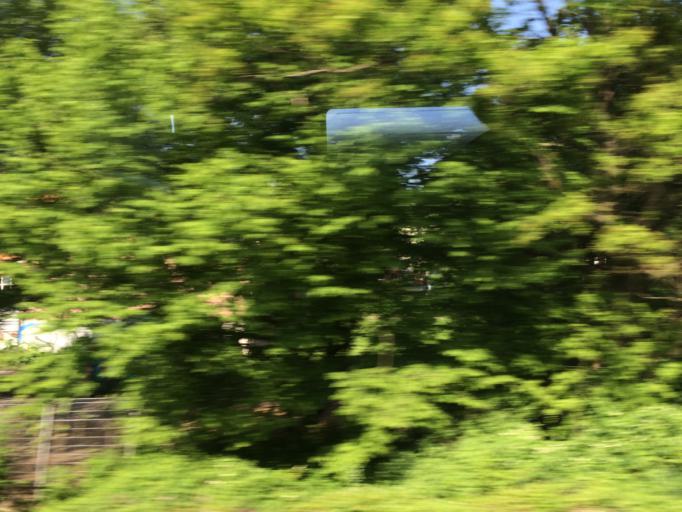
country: DE
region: North Rhine-Westphalia
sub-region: Regierungsbezirk Dusseldorf
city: Dusseldorf
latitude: 51.1991
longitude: 6.8347
